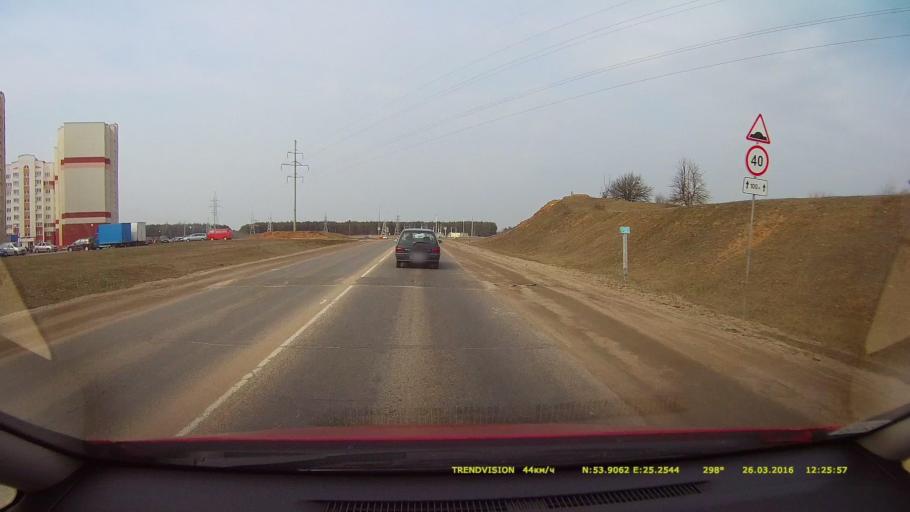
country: BY
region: Grodnenskaya
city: Lida
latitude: 53.9063
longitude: 25.2542
